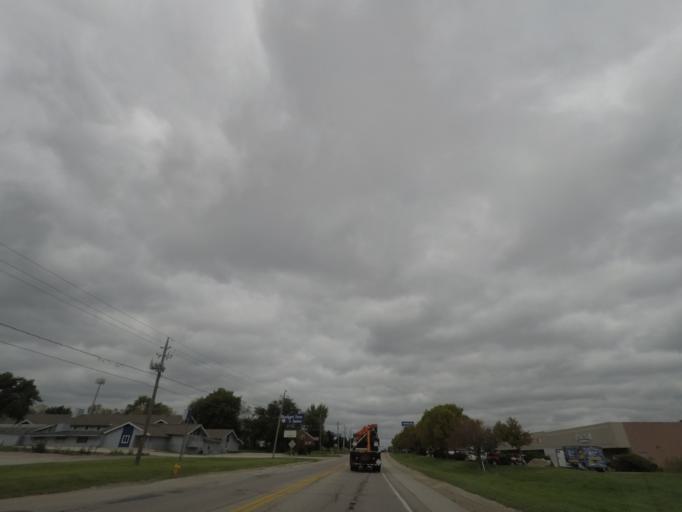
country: US
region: Iowa
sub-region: Polk County
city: Saylorville
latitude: 41.6546
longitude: -93.6005
